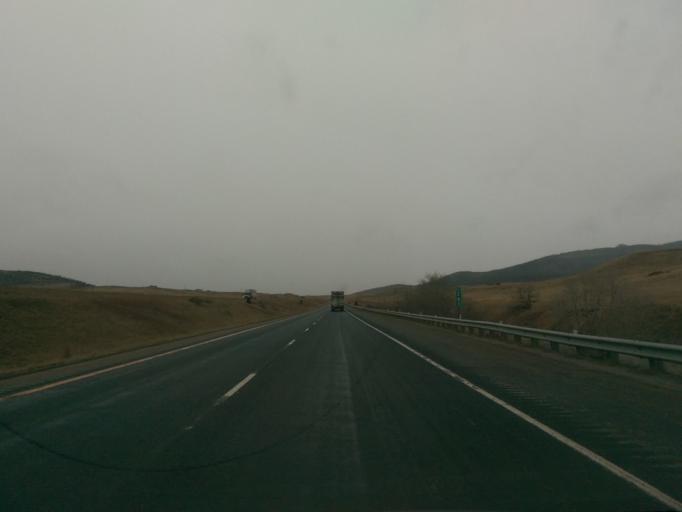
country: US
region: Montana
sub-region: Jefferson County
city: Whitehall
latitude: 45.8965
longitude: -111.8350
